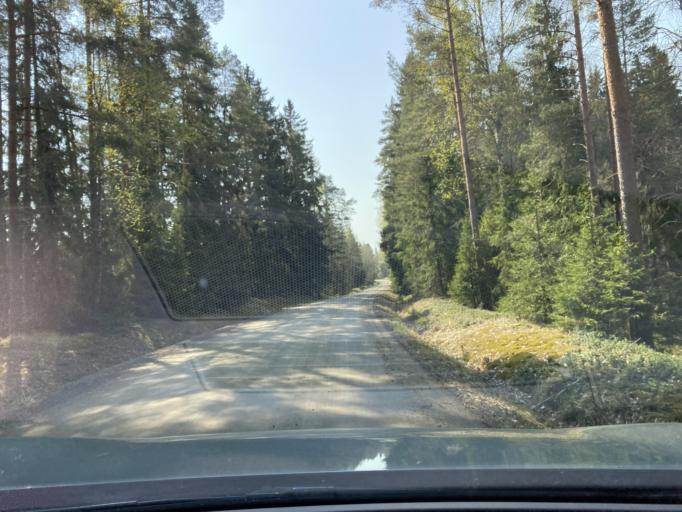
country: FI
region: Satakunta
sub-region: Pori
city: Huittinen
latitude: 61.1388
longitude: 22.8331
